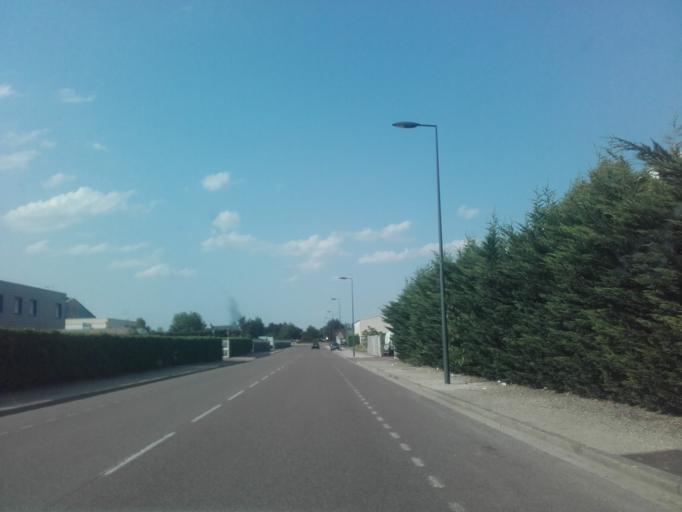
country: FR
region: Bourgogne
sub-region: Departement de la Cote-d'Or
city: Beaune
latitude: 47.0217
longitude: 4.8653
